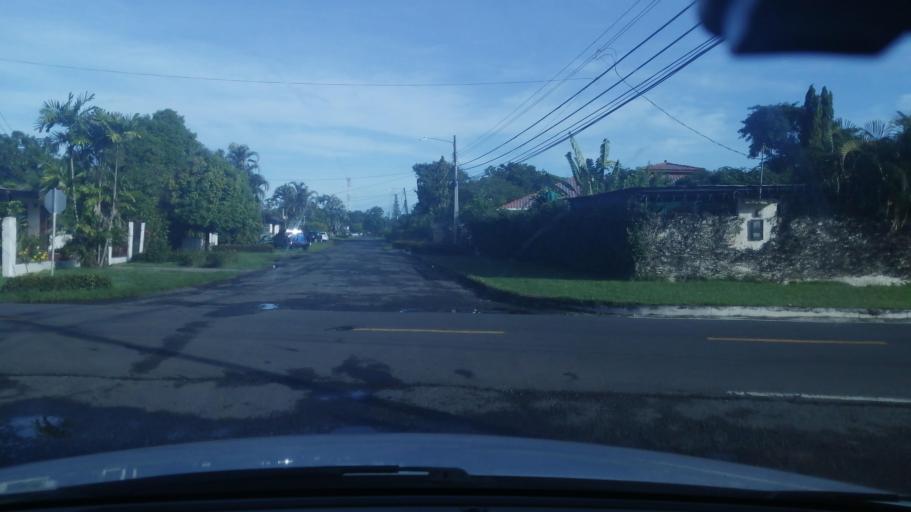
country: PA
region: Chiriqui
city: David
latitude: 8.4411
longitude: -82.4255
